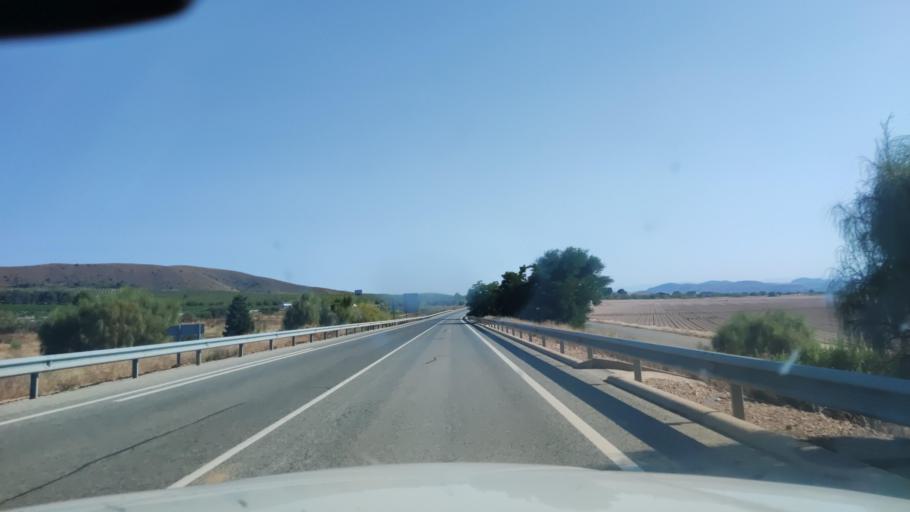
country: ES
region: Castille-La Mancha
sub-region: Provincia de Albacete
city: Tobarra
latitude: 38.6333
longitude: -1.6685
